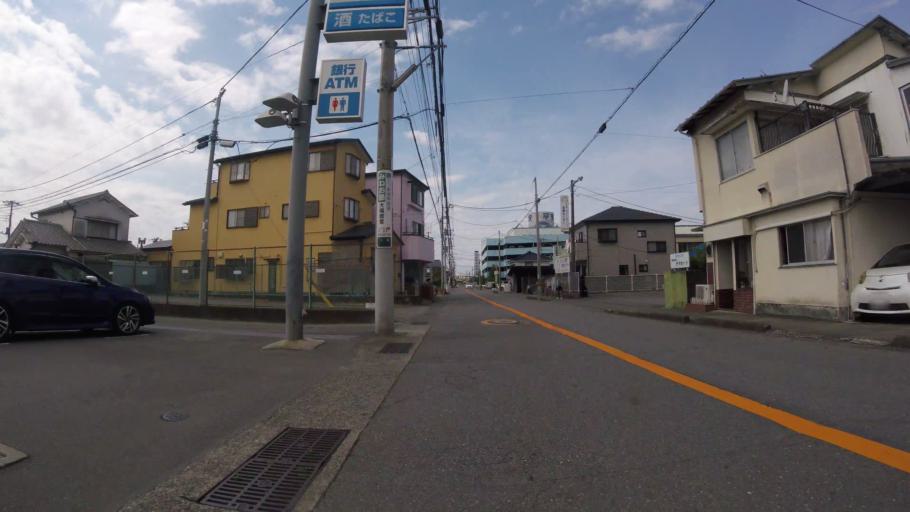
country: JP
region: Shizuoka
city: Numazu
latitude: 35.1164
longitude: 138.8777
